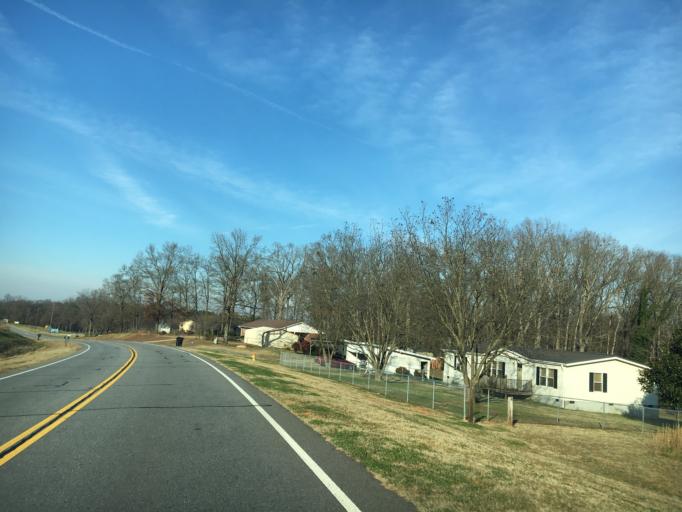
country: US
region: Georgia
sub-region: Franklin County
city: Lavonia
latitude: 34.4021
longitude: -83.0222
